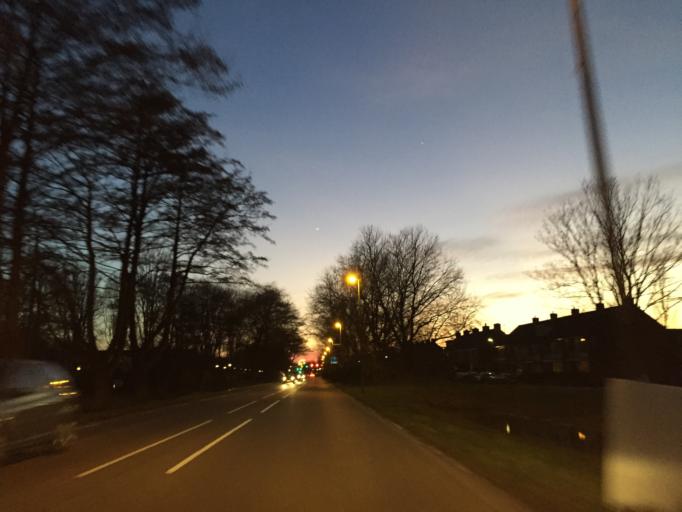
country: NL
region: South Holland
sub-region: Gemeente Leiderdorp
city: Leiderdorp
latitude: 52.1549
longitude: 4.5304
